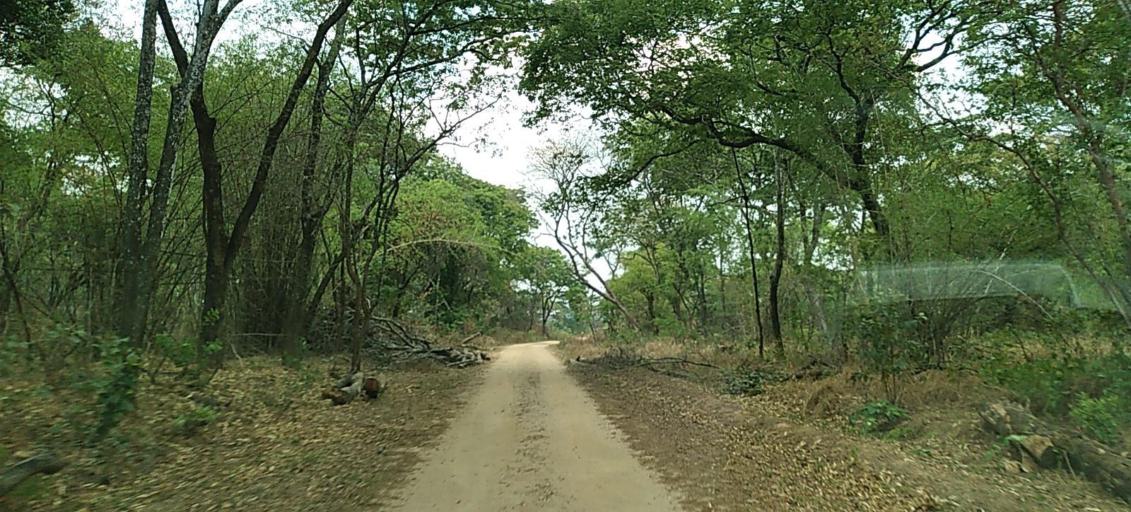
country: ZM
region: Copperbelt
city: Chingola
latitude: -12.7540
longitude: 27.7185
